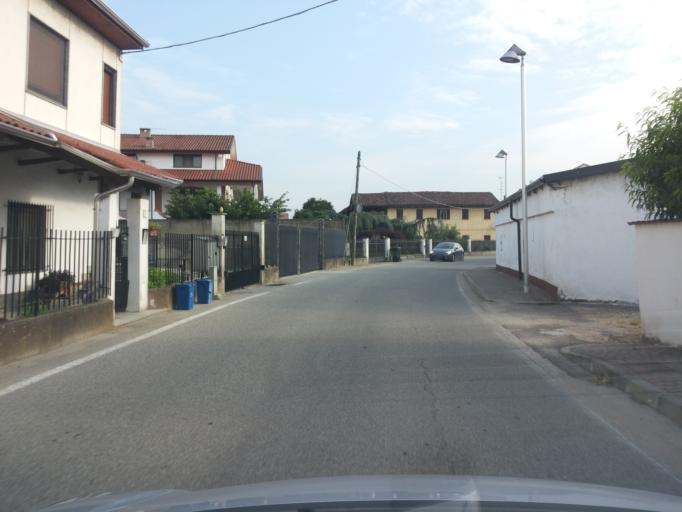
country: IT
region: Piedmont
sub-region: Provincia di Vercelli
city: Pezzana
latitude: 45.2615
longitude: 8.4784
